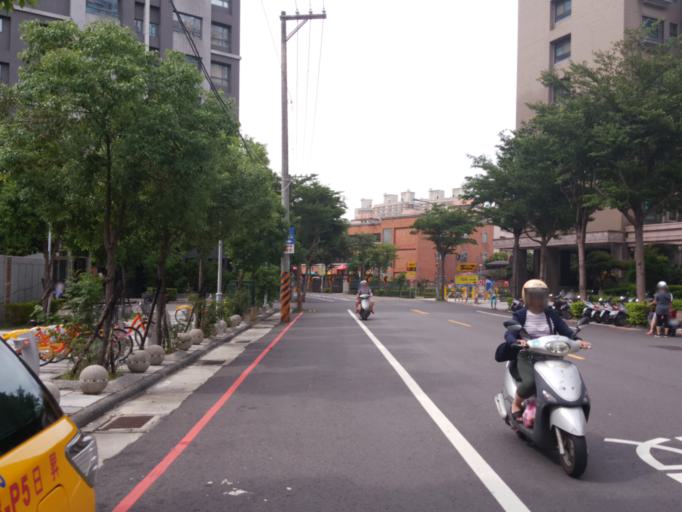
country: TW
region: Taiwan
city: Taoyuan City
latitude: 25.0559
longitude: 121.2946
